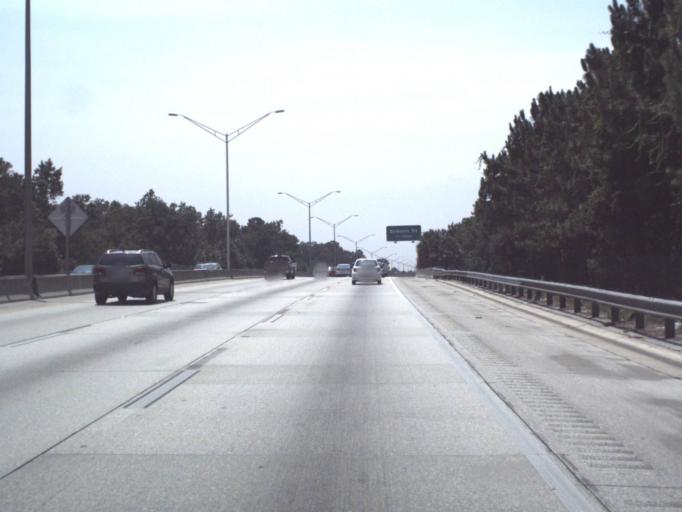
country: US
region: Florida
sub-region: Duval County
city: Jacksonville
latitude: 30.2831
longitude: -81.6222
